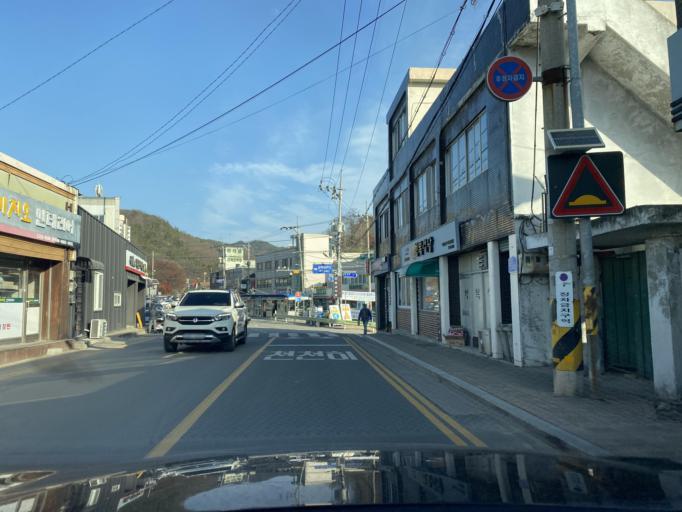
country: KR
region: Chungcheongnam-do
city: Yesan
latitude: 36.6802
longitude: 126.8511
